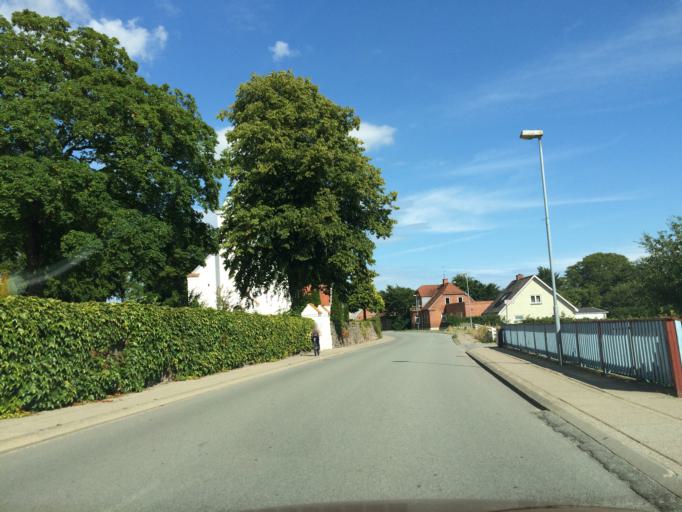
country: DK
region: Central Jutland
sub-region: Syddjurs Kommune
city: Ebeltoft
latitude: 56.3026
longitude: 10.6914
